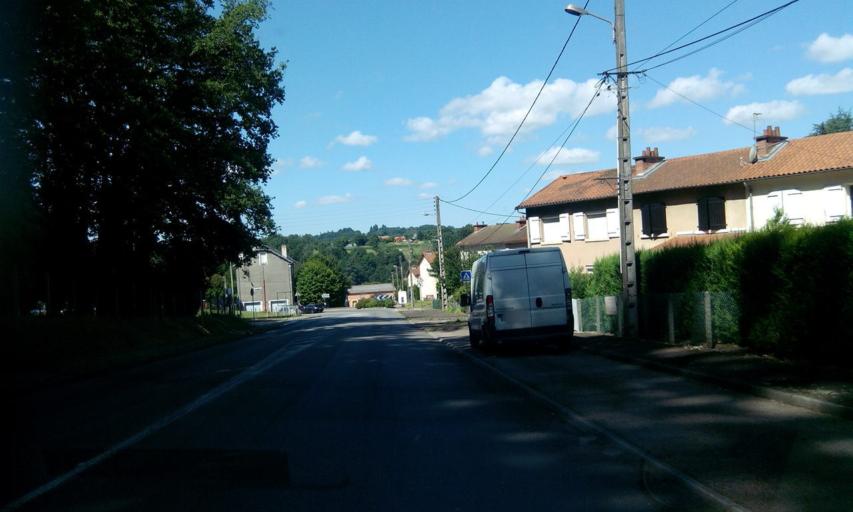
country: FR
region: Limousin
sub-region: Departement de la Haute-Vienne
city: Saint-Leonard-de-Noblat
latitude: 45.8317
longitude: 1.4861
